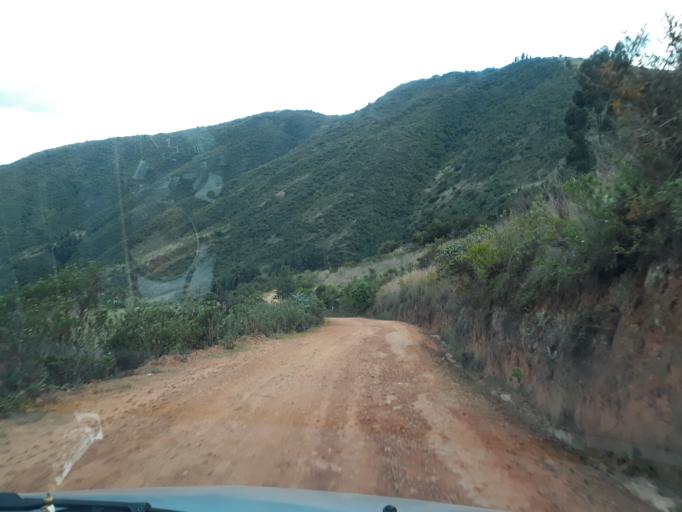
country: CO
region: Boyaca
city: Santa Rosa de Viterbo
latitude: 5.8618
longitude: -72.9688
